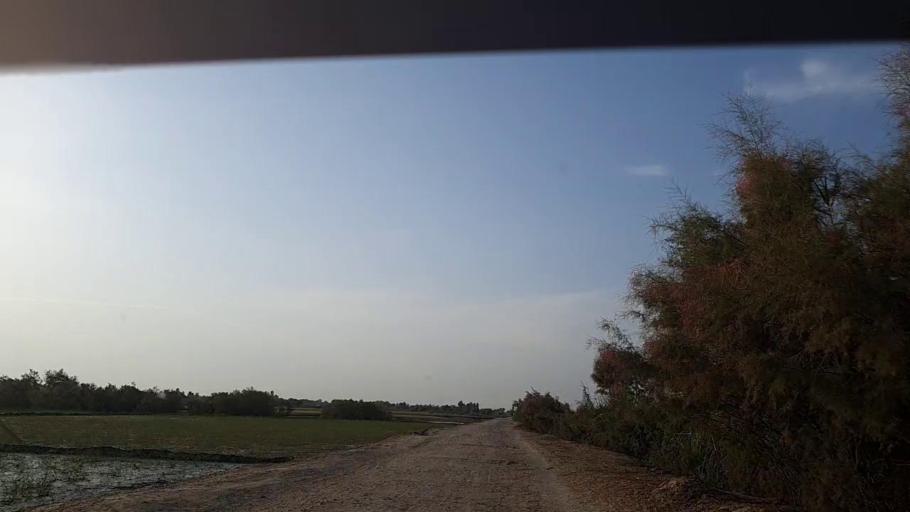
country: PK
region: Sindh
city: Khanpur
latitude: 27.8043
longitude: 69.3113
